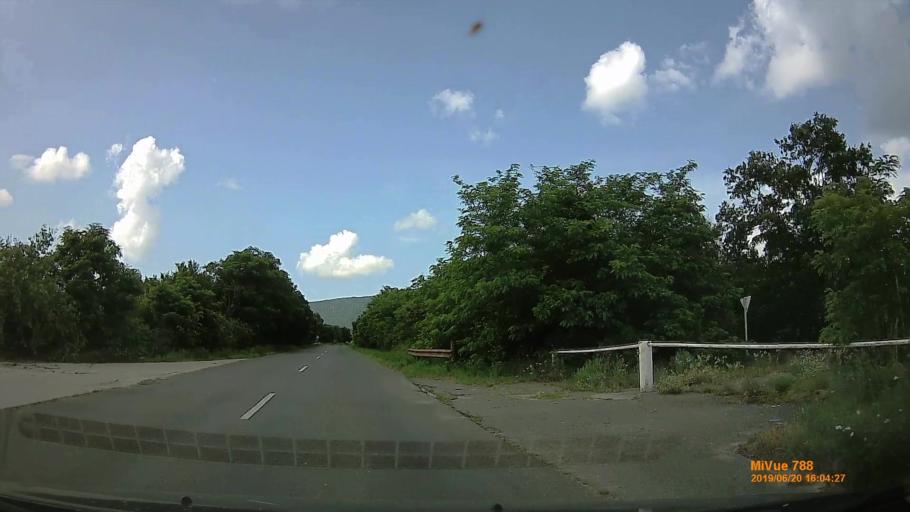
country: HU
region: Baranya
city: Pellerd
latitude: 46.0722
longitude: 18.1152
